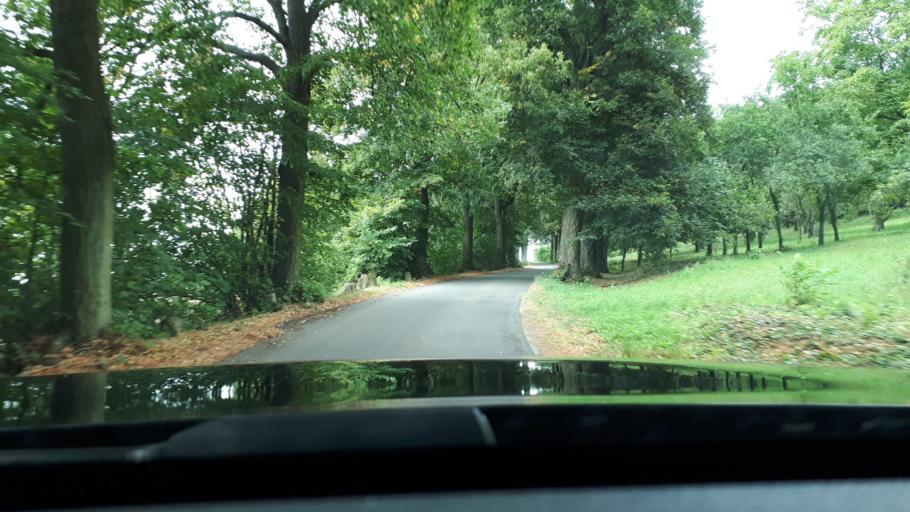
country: PL
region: Lower Silesian Voivodeship
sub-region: Powiat zlotoryjski
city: Olszanica
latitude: 51.1730
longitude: 15.7626
